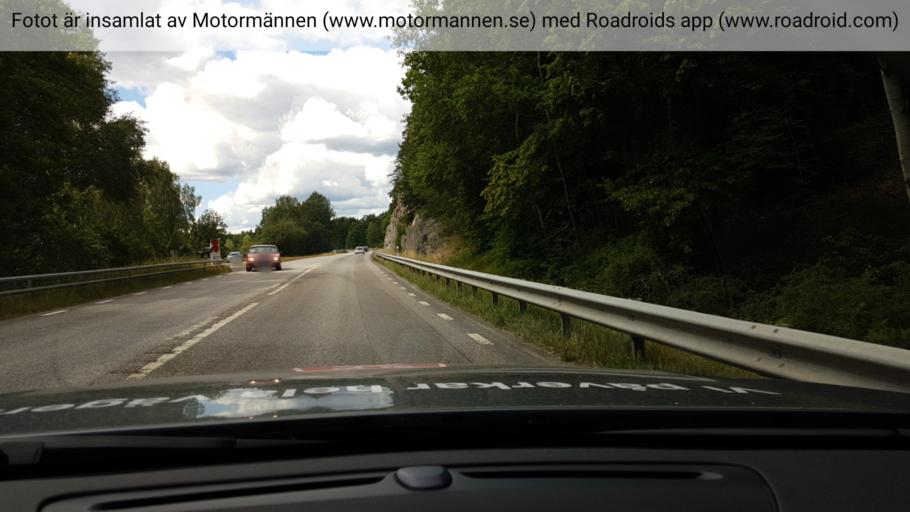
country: SE
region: Stockholm
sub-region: Osterakers Kommun
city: Akersberga
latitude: 59.4263
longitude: 18.2674
